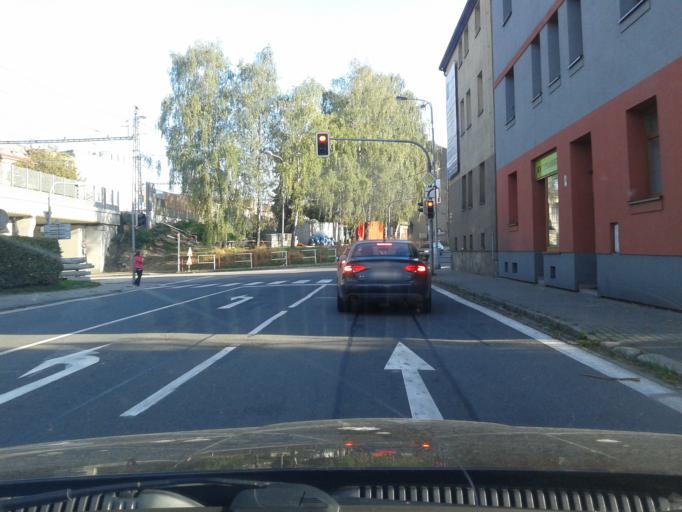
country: CZ
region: Moravskoslezsky
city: Cesky Tesin
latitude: 49.7474
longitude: 18.6205
